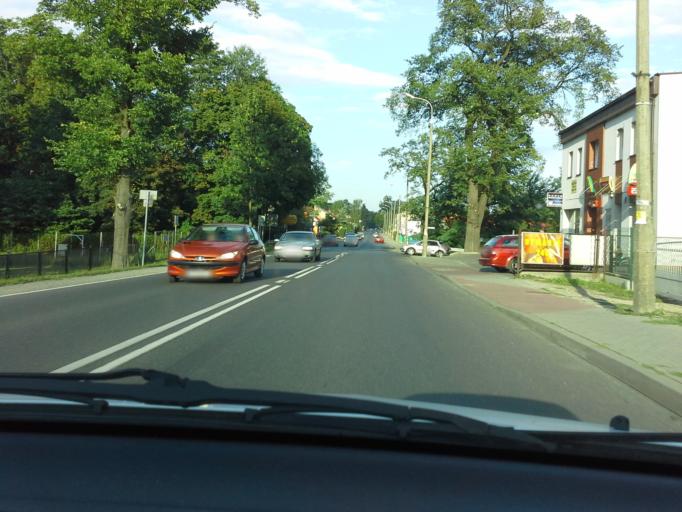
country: PL
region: Lesser Poland Voivodeship
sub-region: Powiat krakowski
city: Tenczynek
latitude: 50.1314
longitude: 19.6177
